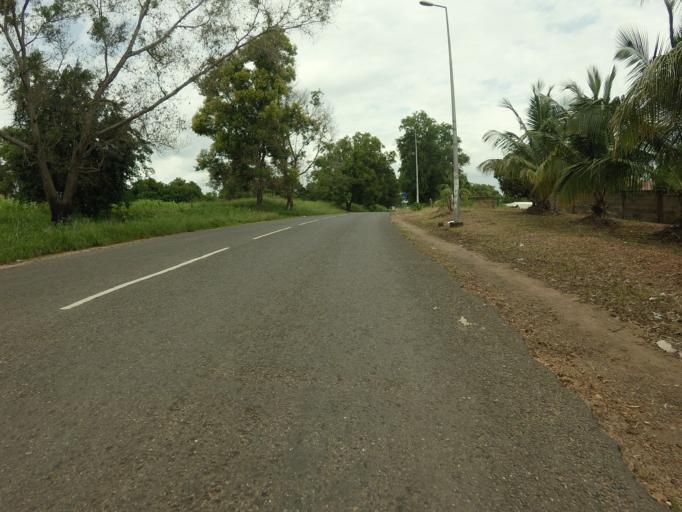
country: GH
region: Volta
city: Ho
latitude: 6.5954
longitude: 0.4632
